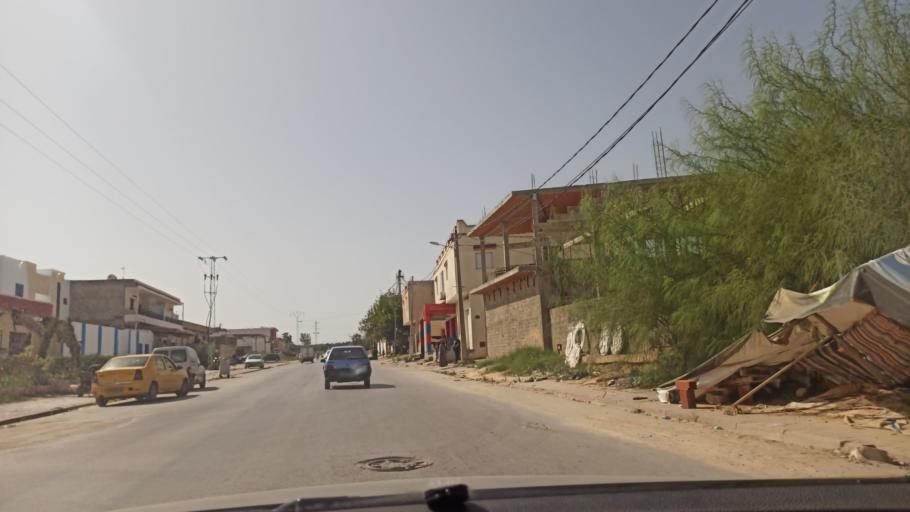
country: TN
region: Manouba
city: Manouba
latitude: 36.7535
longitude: 10.1014
